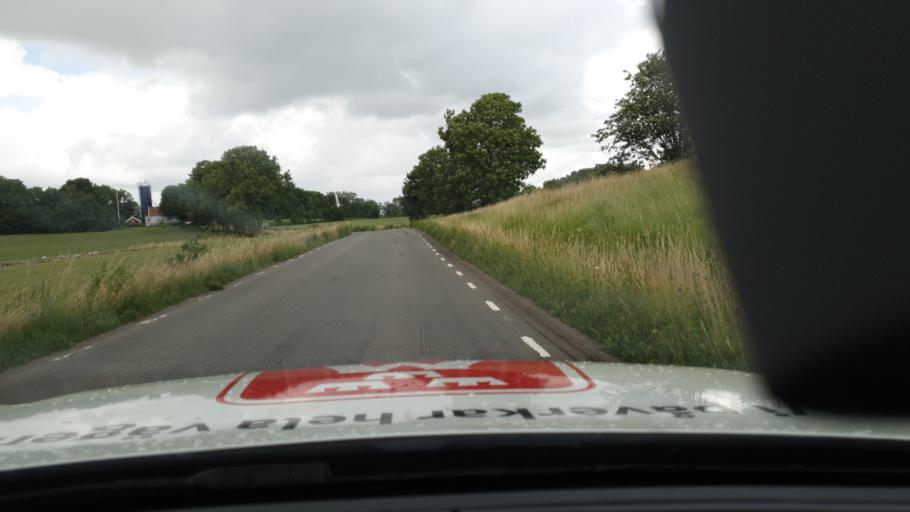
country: SE
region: Vaestra Goetaland
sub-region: Falkopings Kommun
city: Akarp
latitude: 58.2146
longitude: 13.6023
